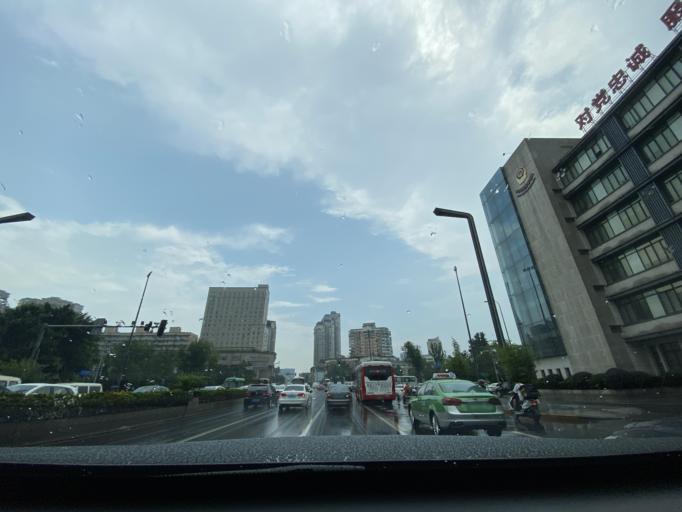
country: CN
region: Sichuan
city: Chengdu
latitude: 30.6493
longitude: 104.0724
